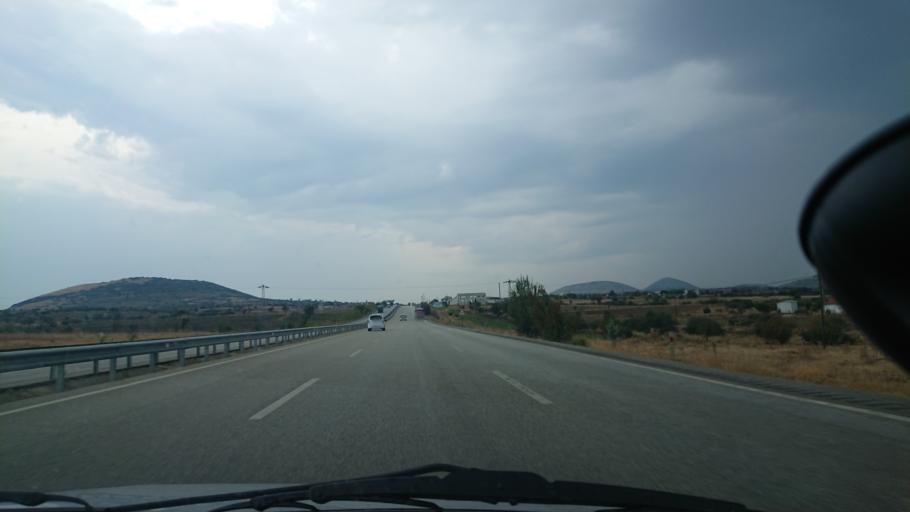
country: TR
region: Manisa
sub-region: Kula
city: Kula
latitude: 38.5659
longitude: 28.7218
